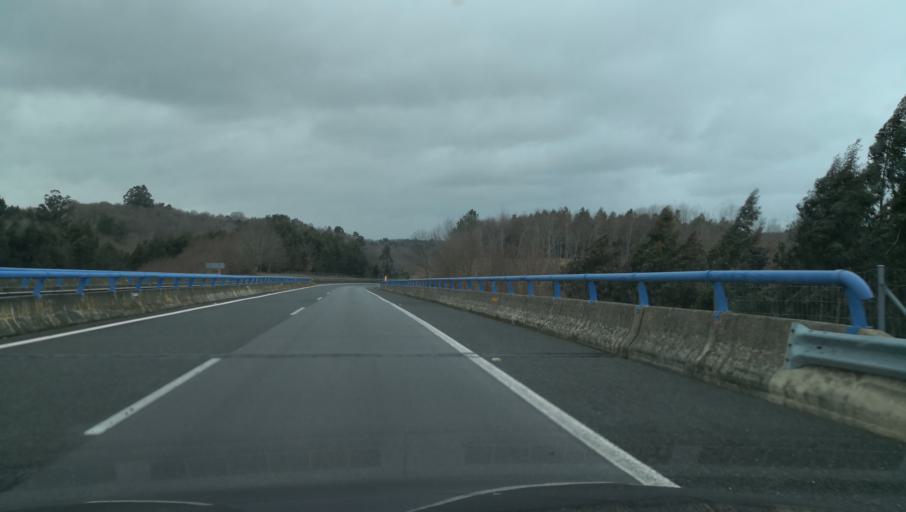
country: ES
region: Galicia
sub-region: Provincia de Pontevedra
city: Lalin
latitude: 42.6610
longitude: -8.1437
